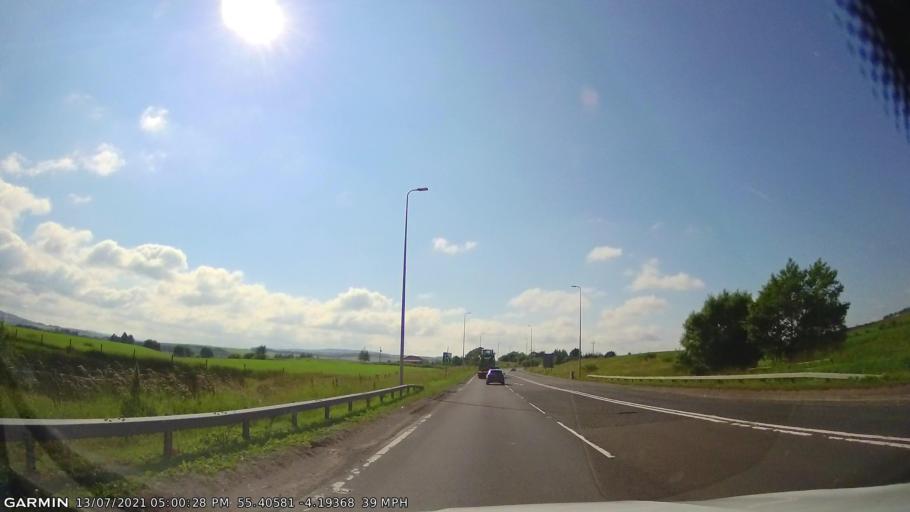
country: GB
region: Scotland
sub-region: East Ayrshire
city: New Cumnock
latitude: 55.4058
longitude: -4.1935
